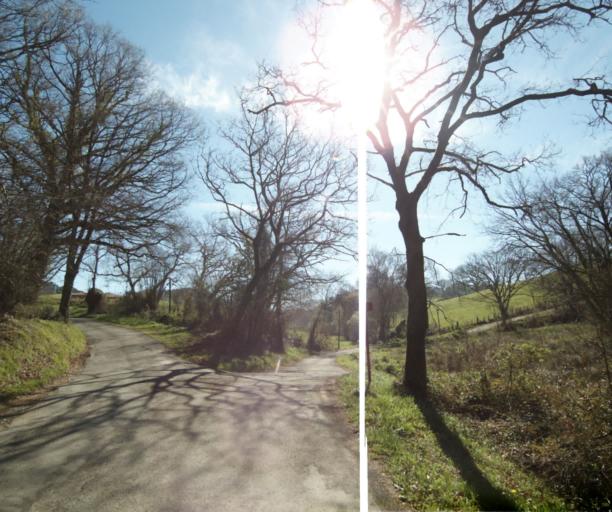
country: FR
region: Aquitaine
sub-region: Departement des Pyrenees-Atlantiques
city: Ciboure
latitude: 43.3637
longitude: -1.6761
